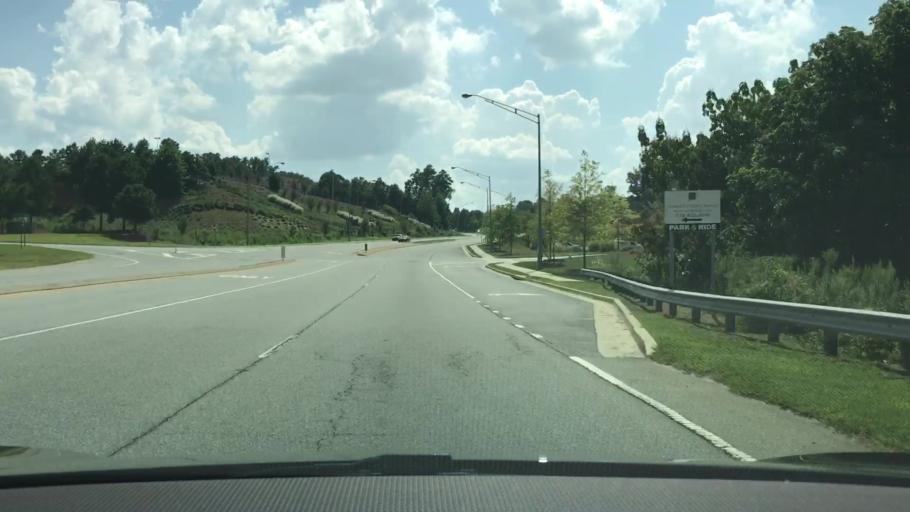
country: US
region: Georgia
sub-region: Gwinnett County
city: Buford
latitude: 34.0878
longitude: -83.9983
